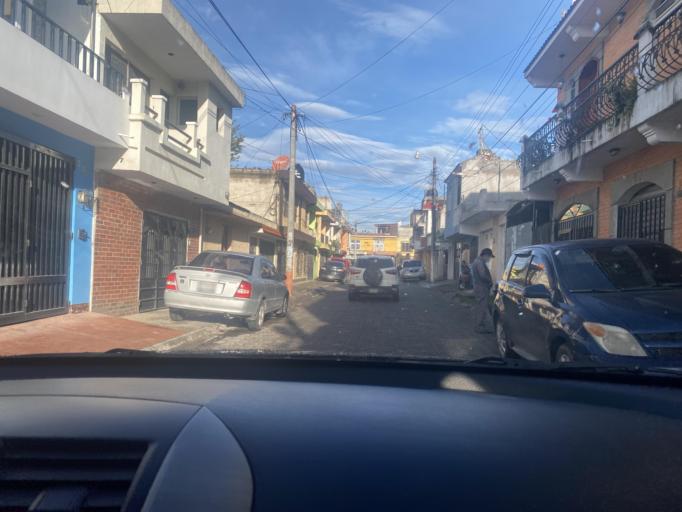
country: GT
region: Quetzaltenango
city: Olintepeque
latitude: 14.8645
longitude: -91.5208
